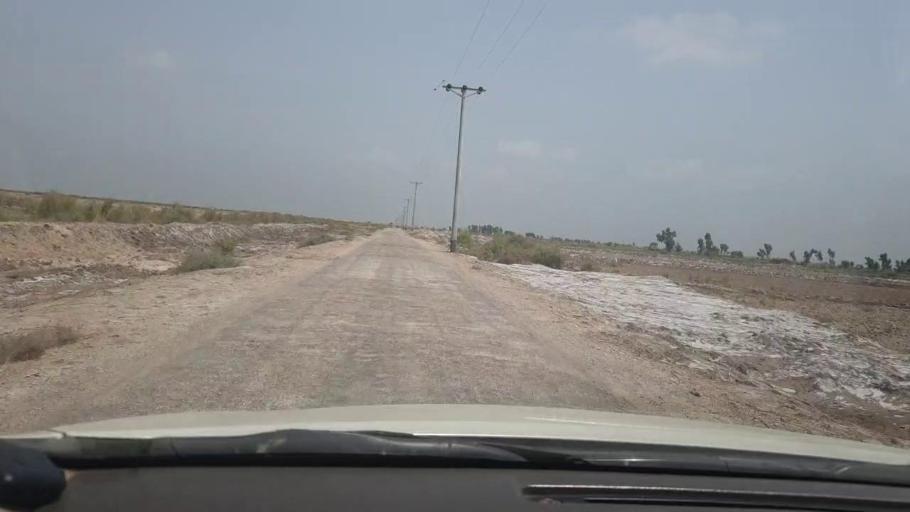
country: PK
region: Sindh
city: Garhi Yasin
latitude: 27.9942
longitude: 68.5011
